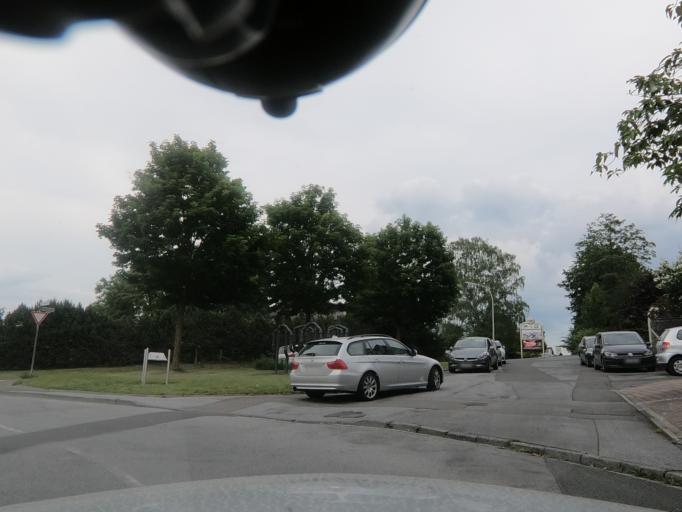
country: DE
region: North Rhine-Westphalia
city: Warstein
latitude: 51.4530
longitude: 8.3623
